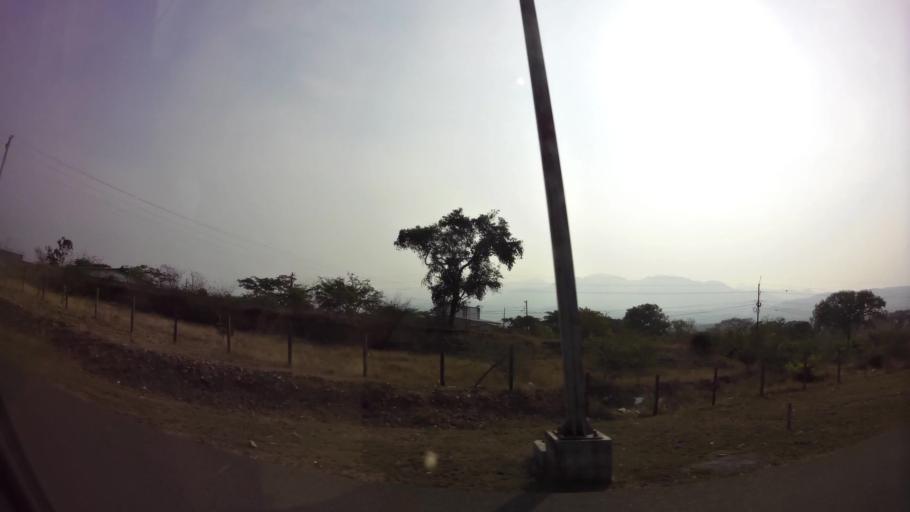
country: HN
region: Comayagua
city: Comayagua
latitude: 14.4211
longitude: -87.6280
